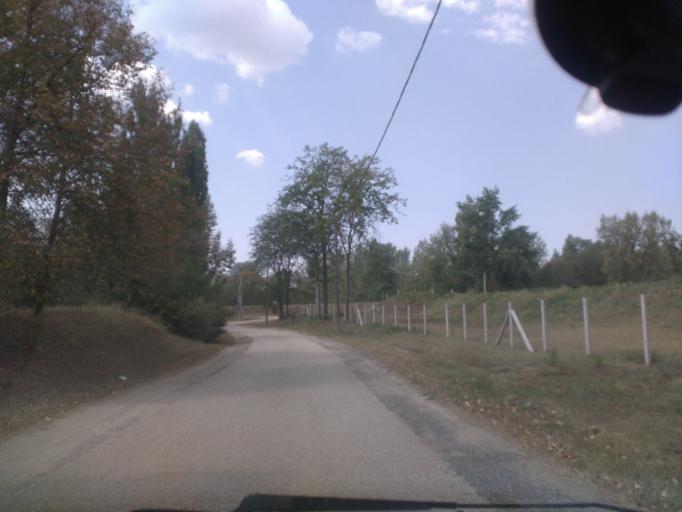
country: HU
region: Komarom-Esztergom
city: Pilismarot
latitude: 47.8002
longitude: 18.8919
